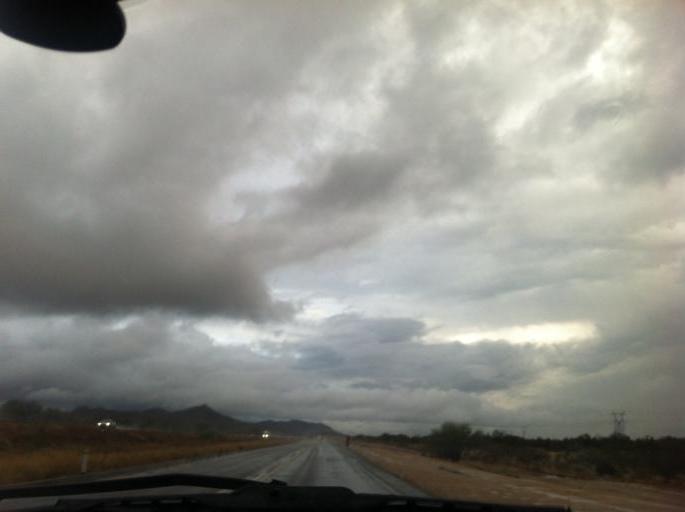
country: MX
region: Sonora
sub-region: San Miguel de Horcasitas
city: Las Mercedes [Agropecuaria]
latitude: 29.4192
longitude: -110.9828
